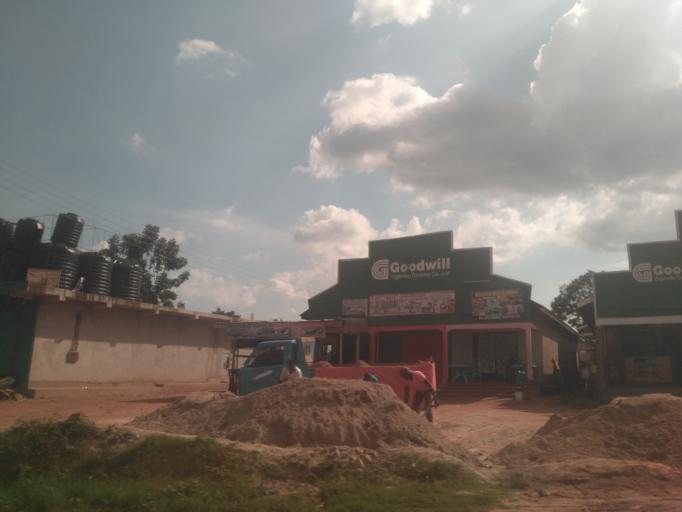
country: UG
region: Central Region
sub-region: Wakiso District
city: Kajansi
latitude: 0.2780
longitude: 32.4764
